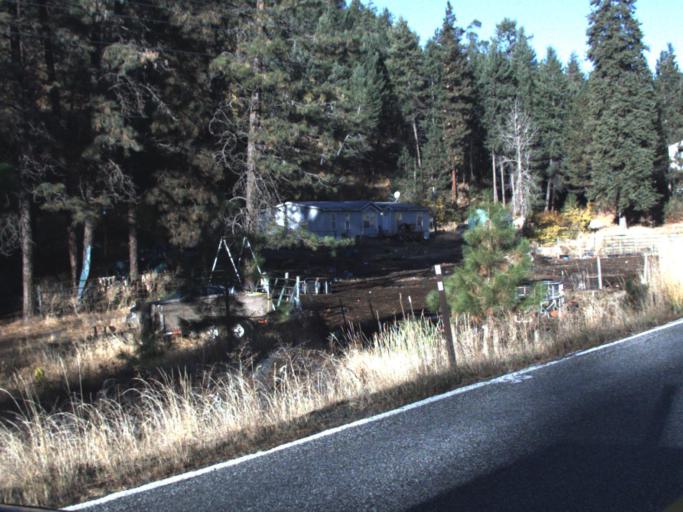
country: US
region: Washington
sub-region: Okanogan County
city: Coulee Dam
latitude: 48.0717
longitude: -118.6763
